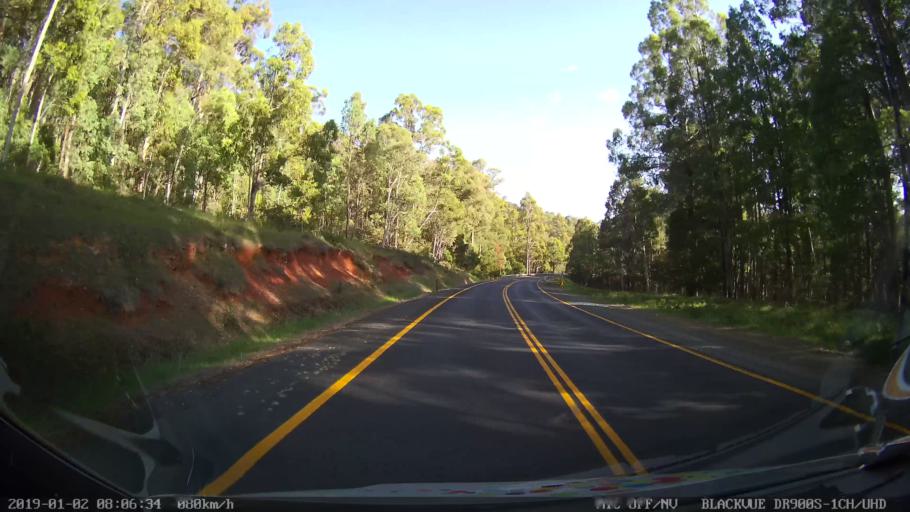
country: AU
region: New South Wales
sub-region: Tumut Shire
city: Tumut
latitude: -35.6385
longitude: 148.3868
